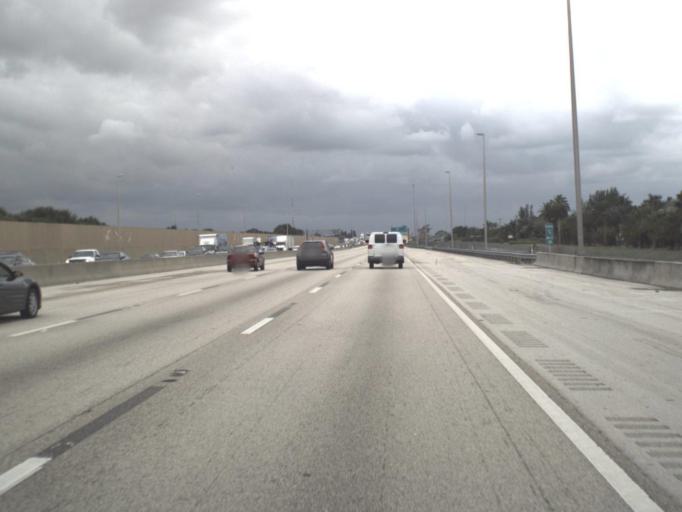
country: US
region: Florida
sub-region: Palm Beach County
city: Villages of Oriole
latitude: 26.5381
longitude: -80.1729
